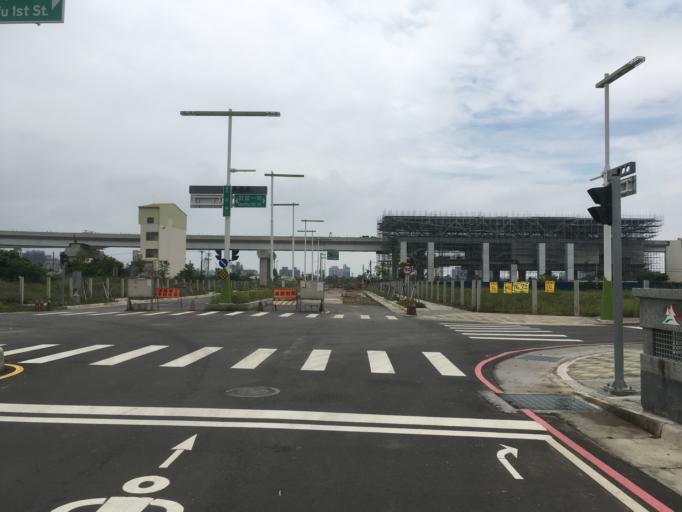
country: TW
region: Taiwan
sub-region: Taichung City
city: Taichung
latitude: 24.1840
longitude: 120.7078
